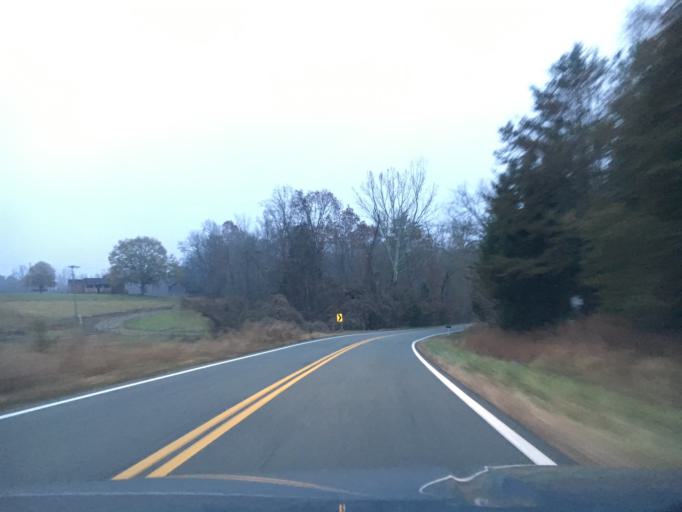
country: US
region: Virginia
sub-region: Halifax County
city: Mountain Road
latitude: 36.6979
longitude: -78.9728
